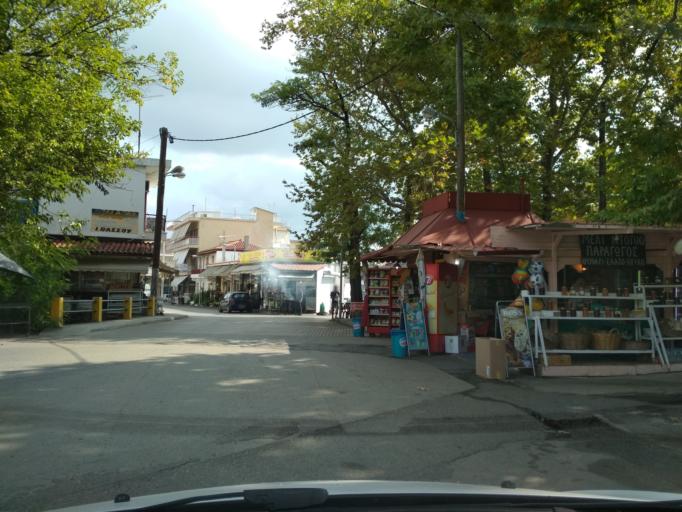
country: GR
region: Central Greece
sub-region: Nomos Evvoias
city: Prokopion
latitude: 38.7335
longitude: 23.4916
